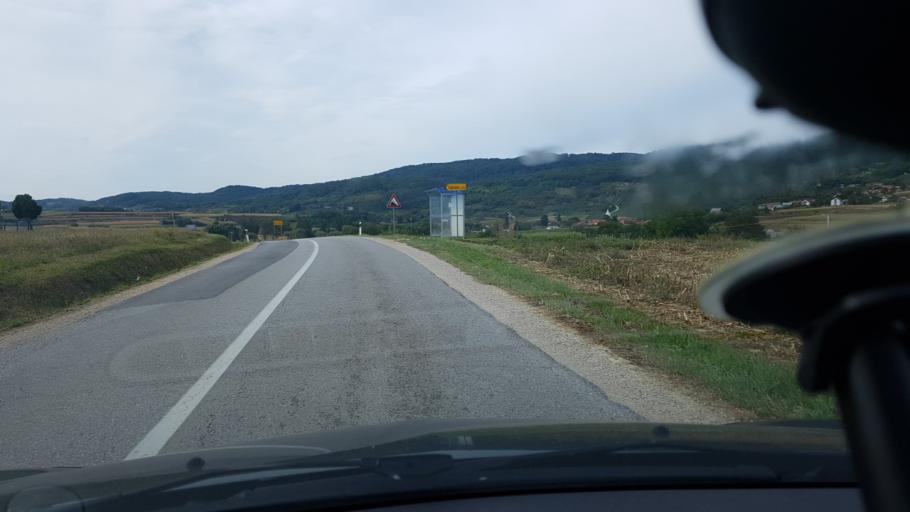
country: HR
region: Varazdinska
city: Ljubescica
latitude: 46.1029
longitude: 16.3996
